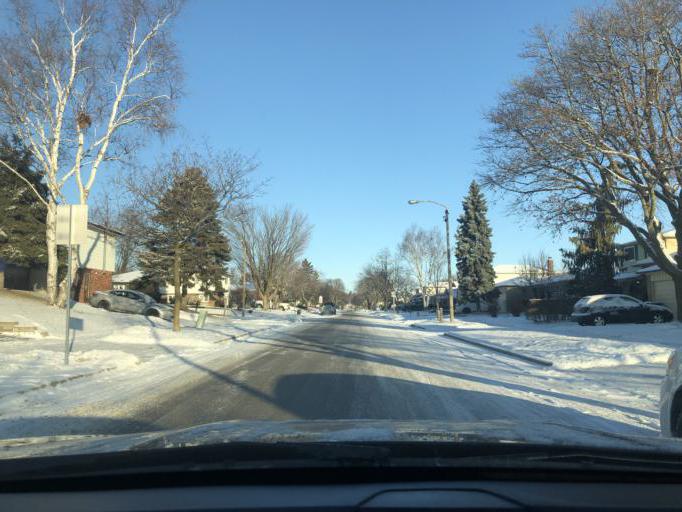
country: CA
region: Ontario
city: Pickering
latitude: 43.7831
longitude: -79.1391
